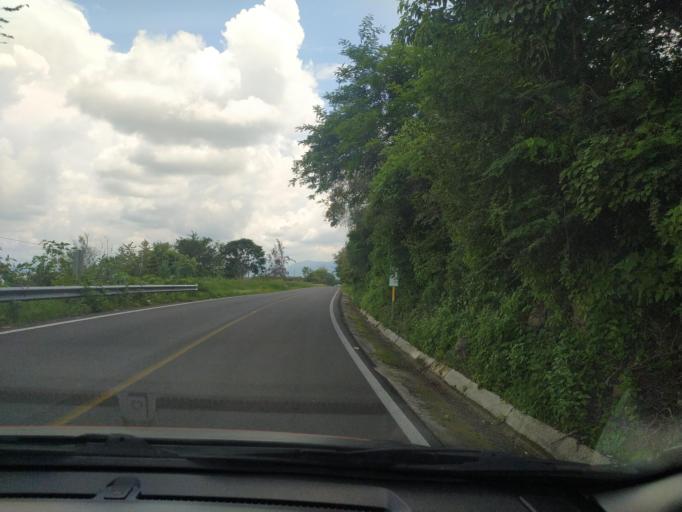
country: MX
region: Jalisco
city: Villa Corona
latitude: 20.3598
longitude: -103.6670
